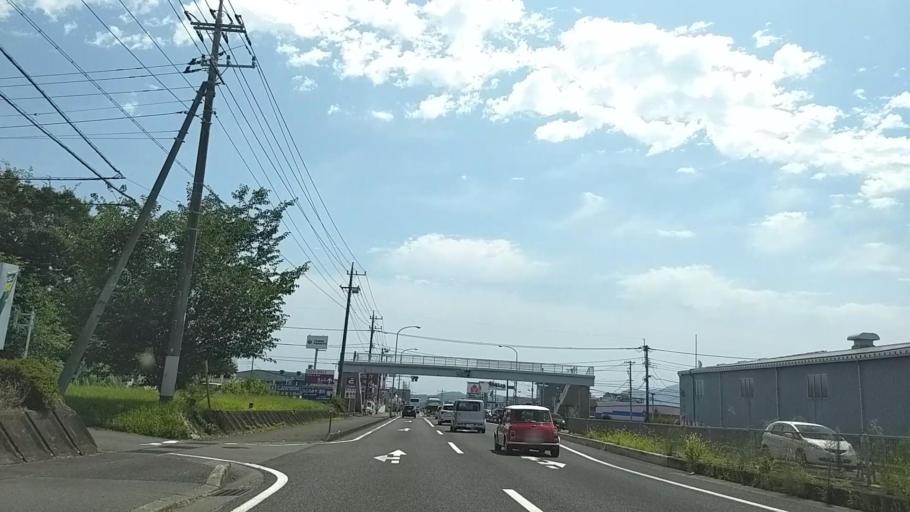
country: JP
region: Shizuoka
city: Fujinomiya
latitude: 35.2511
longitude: 138.6167
